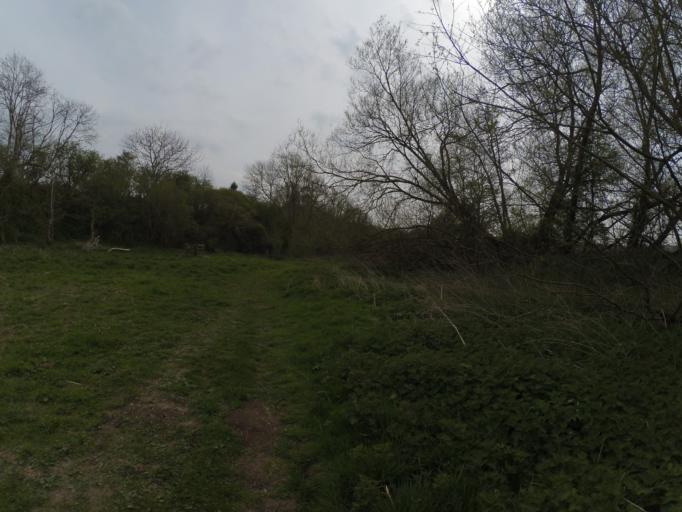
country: GB
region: England
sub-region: West Sussex
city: Arundel
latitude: 50.8711
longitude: -0.5277
